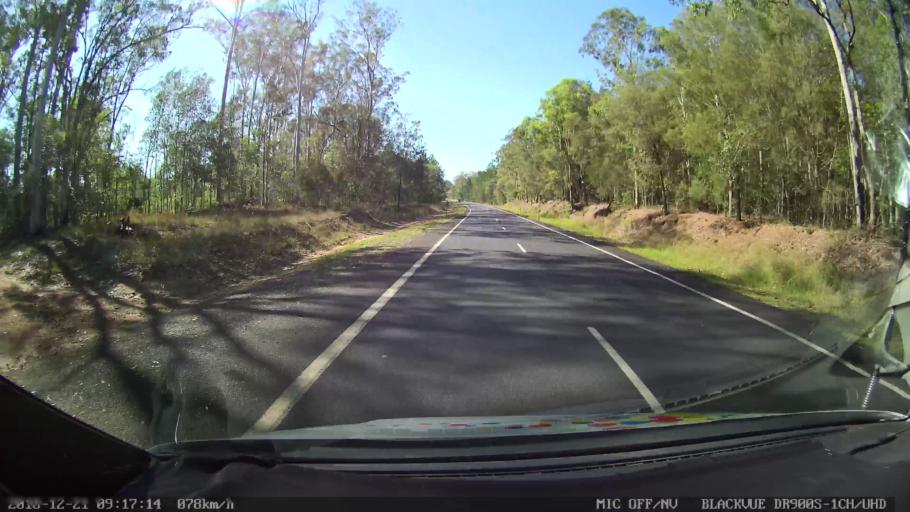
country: AU
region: New South Wales
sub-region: Clarence Valley
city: Maclean
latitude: -29.2899
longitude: 152.9898
